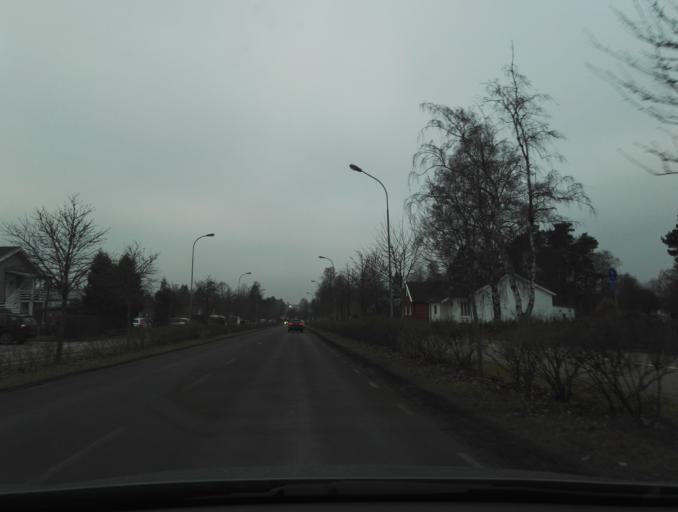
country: SE
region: Kronoberg
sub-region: Vaxjo Kommun
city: Vaexjoe
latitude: 56.8889
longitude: 14.7884
